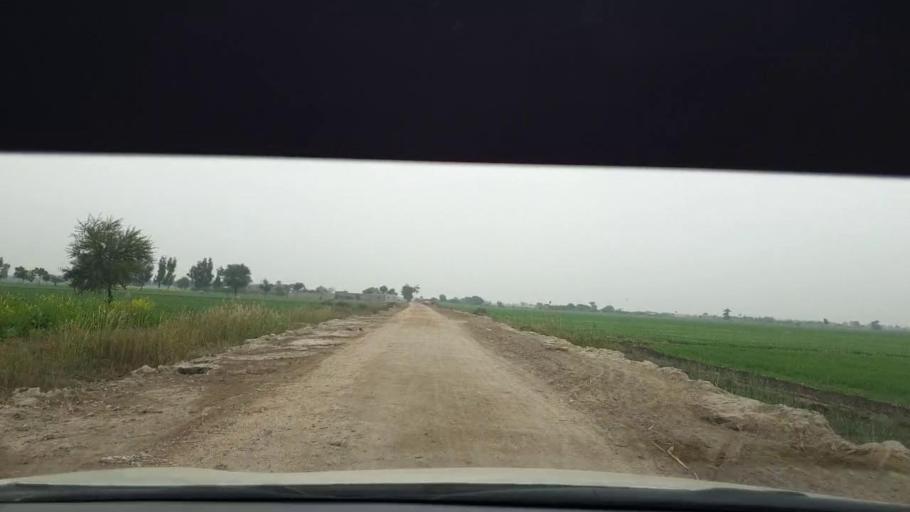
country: PK
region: Sindh
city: Berani
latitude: 25.7594
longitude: 68.8528
